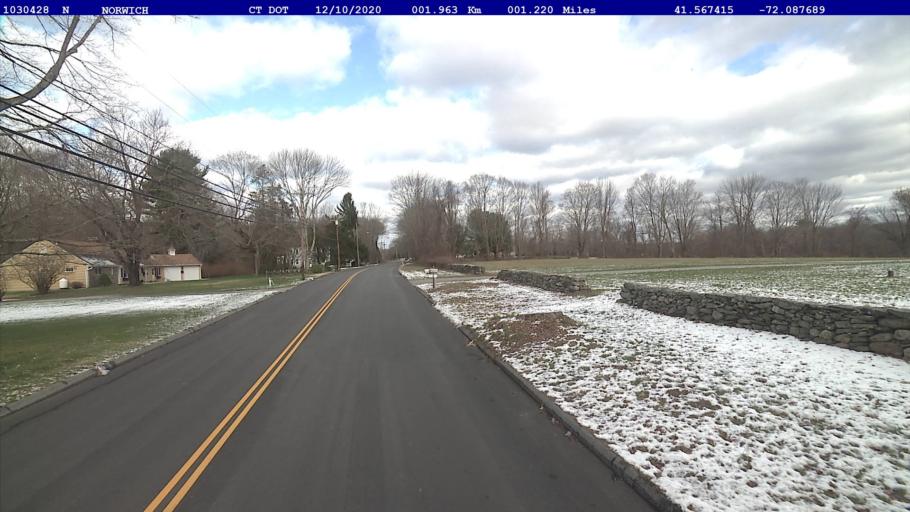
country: US
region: Connecticut
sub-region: New London County
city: Norwich
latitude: 41.5674
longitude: -72.0877
